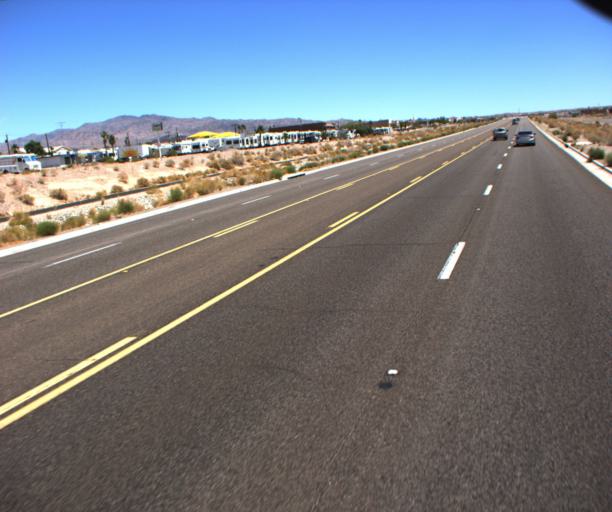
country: US
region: Arizona
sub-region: Mohave County
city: Lake Havasu City
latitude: 34.4556
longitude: -114.2914
